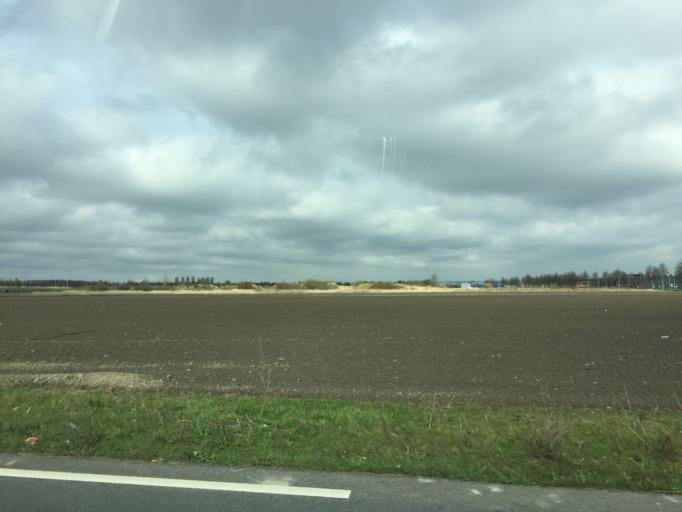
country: NL
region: North Holland
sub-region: Gemeente Aalsmeer
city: Aalsmeer
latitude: 52.2837
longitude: 4.7574
